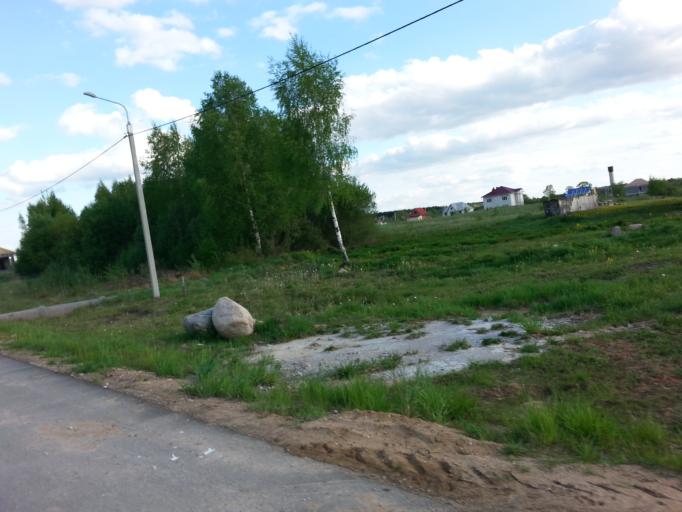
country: BY
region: Minsk
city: Narach
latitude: 54.9404
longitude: 26.6962
